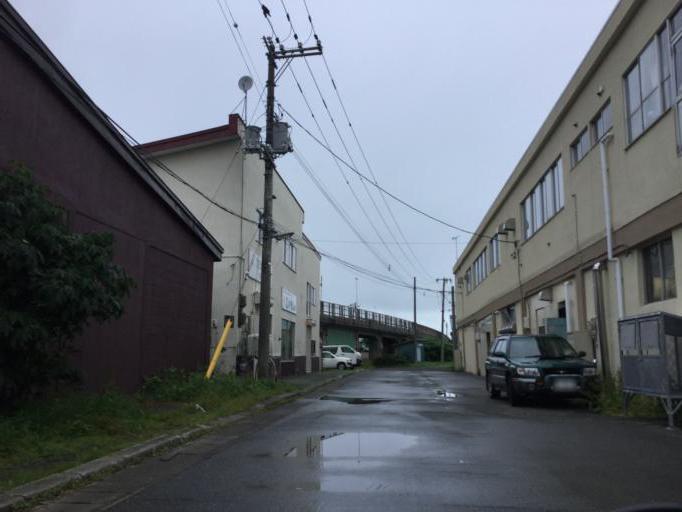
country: JP
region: Hokkaido
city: Wakkanai
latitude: 45.4098
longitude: 141.6766
